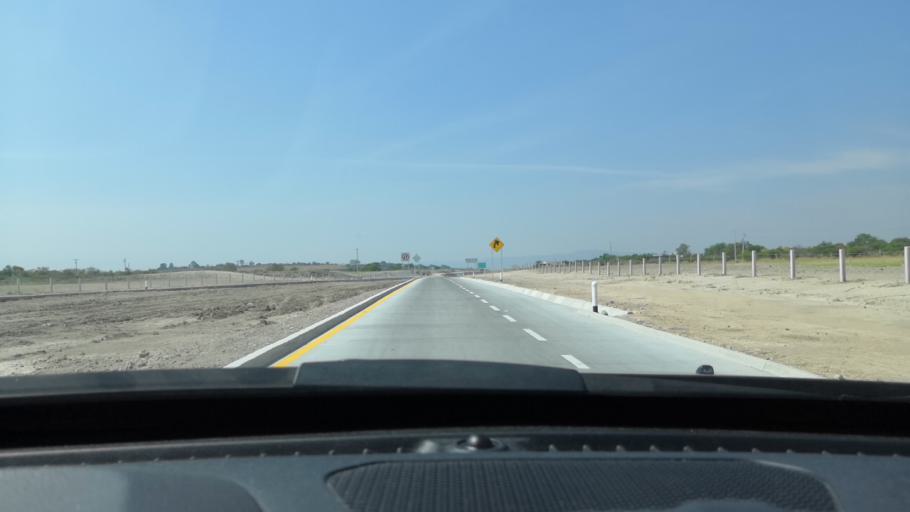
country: MX
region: Guanajuato
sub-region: Leon
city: Malagana (San Antonio del Monte)
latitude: 21.0925
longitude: -101.7910
